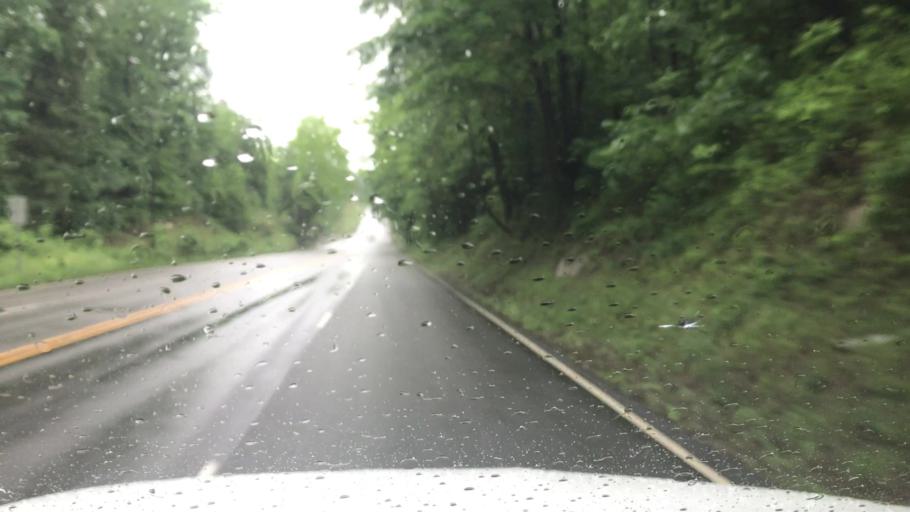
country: US
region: Virginia
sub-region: Hanover County
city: Ashland
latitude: 37.8287
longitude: -77.4704
